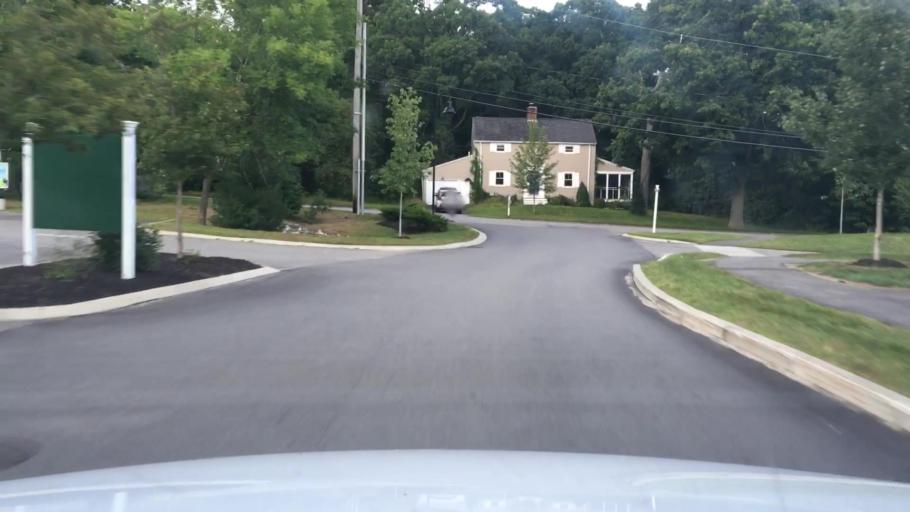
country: US
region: Maine
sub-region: Cumberland County
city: Falmouth
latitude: 43.7258
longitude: -70.2474
